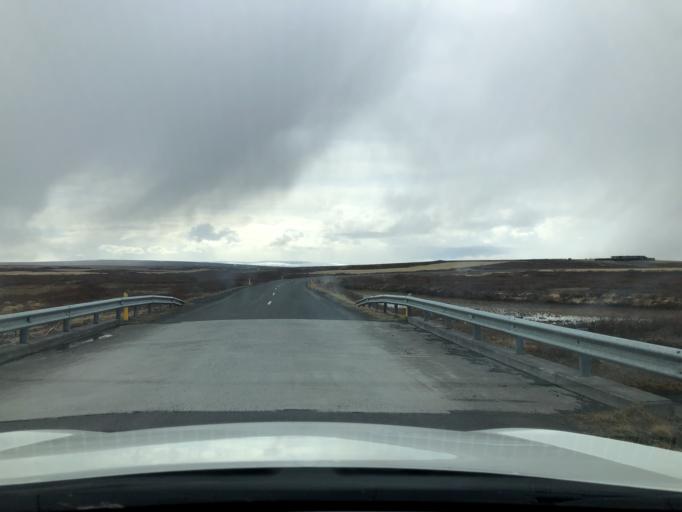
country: IS
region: Northeast
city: Laugar
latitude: 65.5713
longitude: -17.0708
